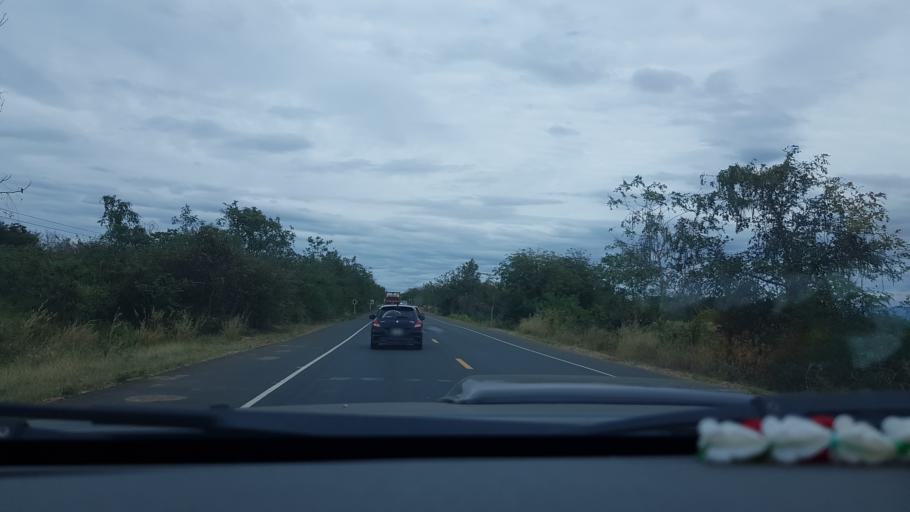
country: TH
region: Phetchabun
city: Phetchabun
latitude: 16.4686
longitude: 101.1262
